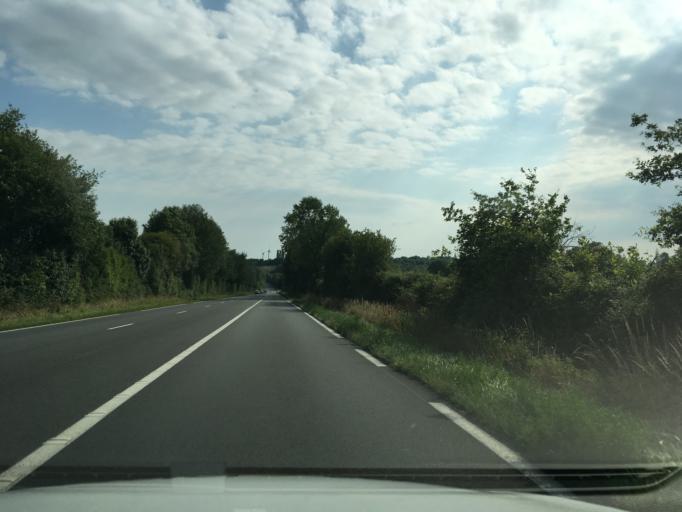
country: FR
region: Poitou-Charentes
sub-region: Departement des Deux-Sevres
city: Champdeniers-Saint-Denis
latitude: 46.4867
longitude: -0.3534
